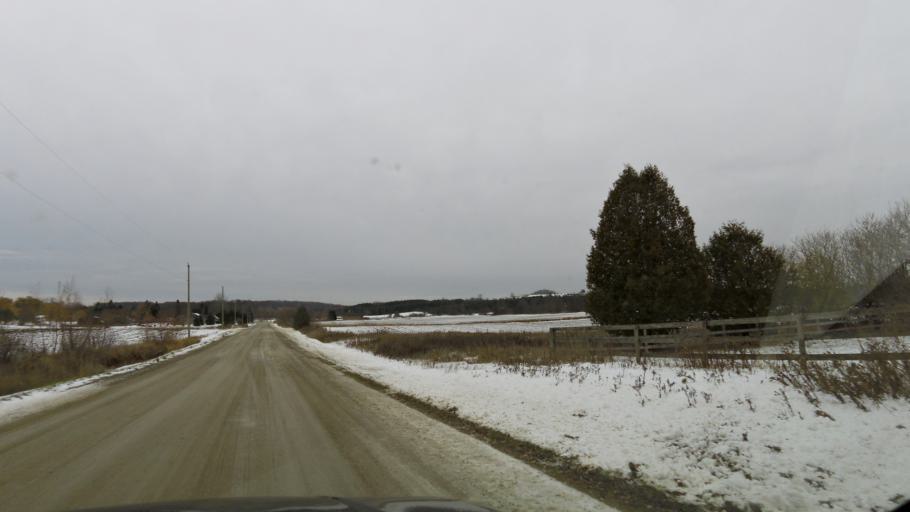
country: CA
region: Ontario
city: Bradford West Gwillimbury
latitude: 43.9836
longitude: -79.6271
